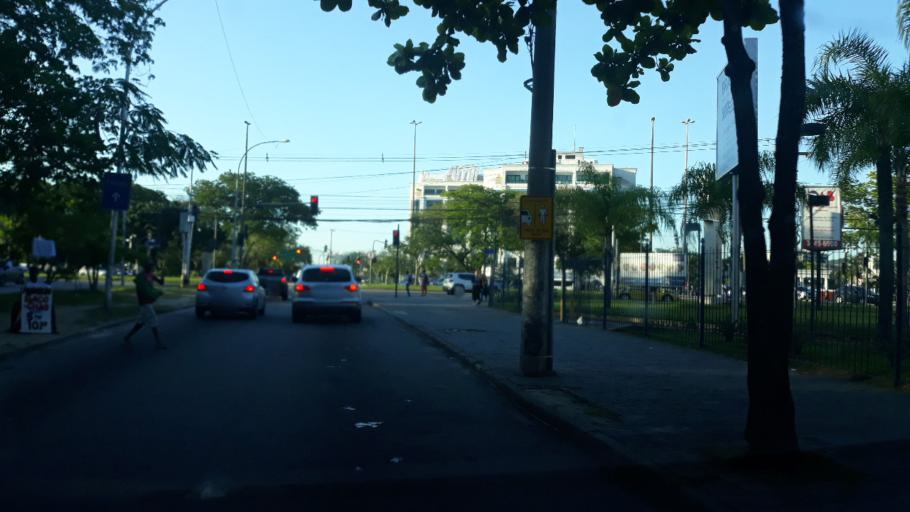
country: BR
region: Rio de Janeiro
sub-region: Rio De Janeiro
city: Rio de Janeiro
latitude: -23.0009
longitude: -43.3533
